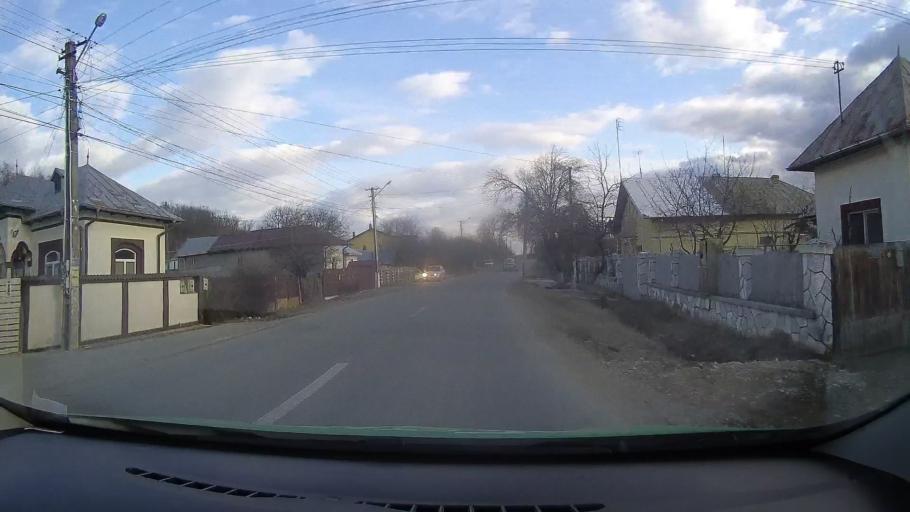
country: RO
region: Dambovita
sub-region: Comuna Gura Ocnitei
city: Gura Ocnitei
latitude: 44.9513
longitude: 25.5566
